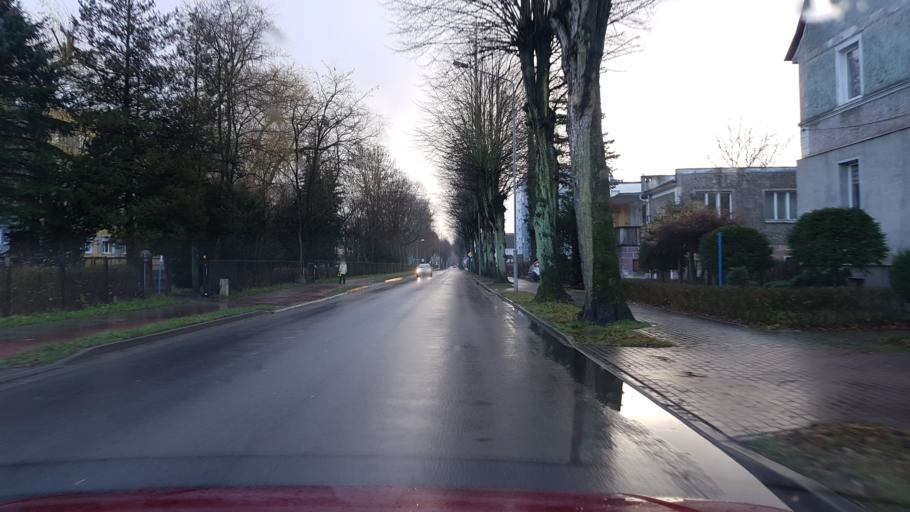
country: PL
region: West Pomeranian Voivodeship
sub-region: Powiat bialogardzki
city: Bialogard
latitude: 54.0127
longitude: 15.9902
